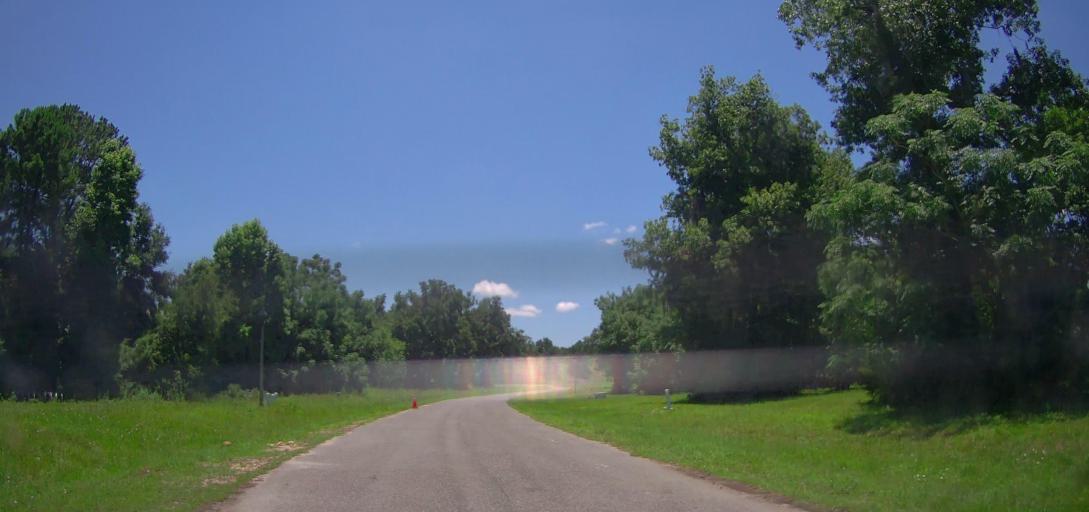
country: US
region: Florida
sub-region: Marion County
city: Belleview
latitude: 29.0906
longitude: -82.0741
